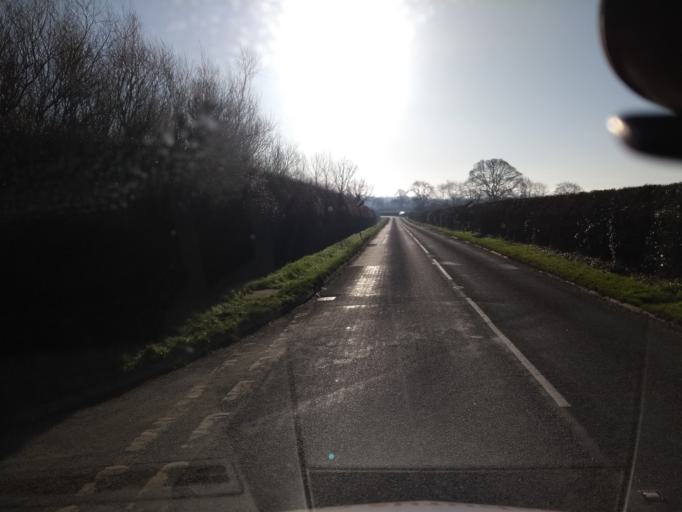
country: GB
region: England
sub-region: Somerset
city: Wincanton
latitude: 51.0827
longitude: -2.3901
